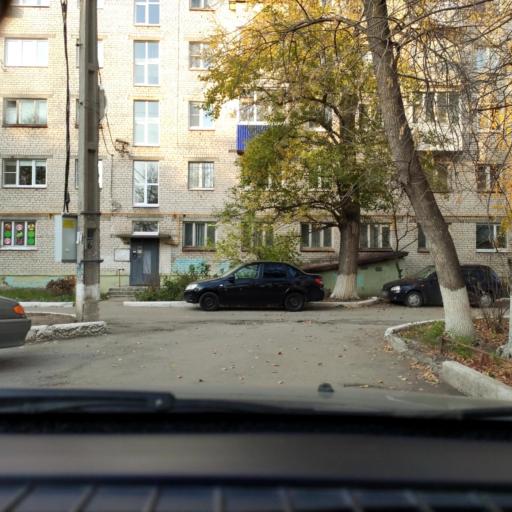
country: RU
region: Samara
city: Tol'yatti
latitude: 53.5027
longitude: 49.4031
